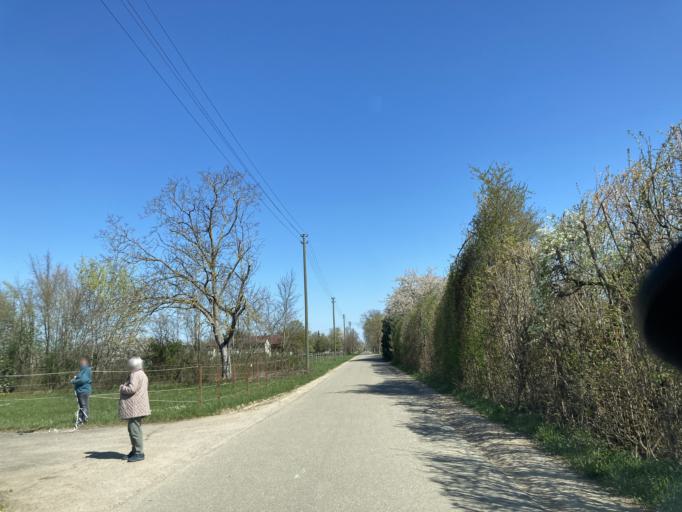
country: DE
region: Baden-Wuerttemberg
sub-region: Freiburg Region
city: Schliengen
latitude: 47.7787
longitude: 7.5626
